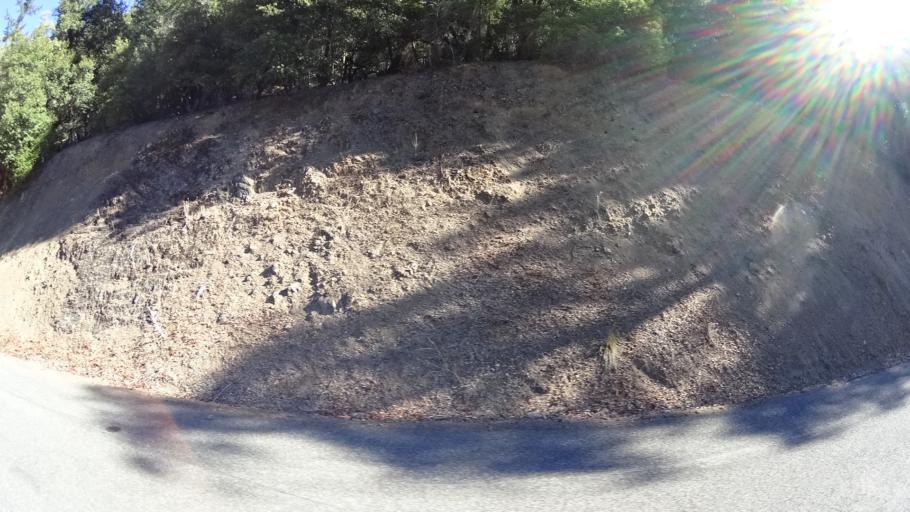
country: US
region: California
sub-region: Humboldt County
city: Willow Creek
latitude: 41.1967
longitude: -123.2152
